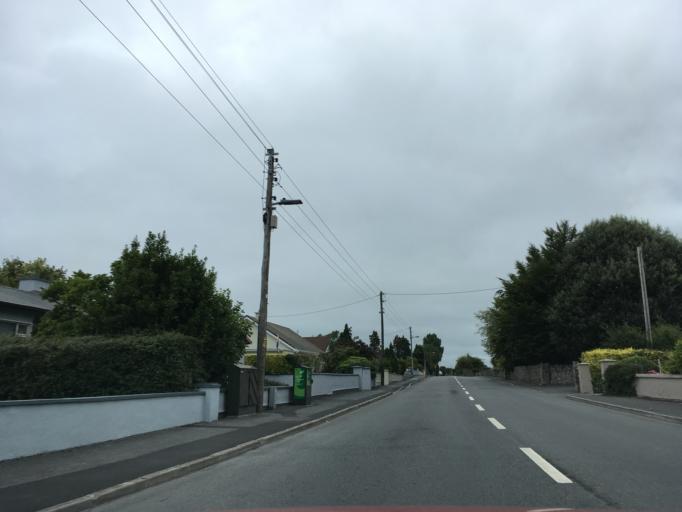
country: IE
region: Munster
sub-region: An Clar
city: Ennis
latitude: 52.8332
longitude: -8.9916
